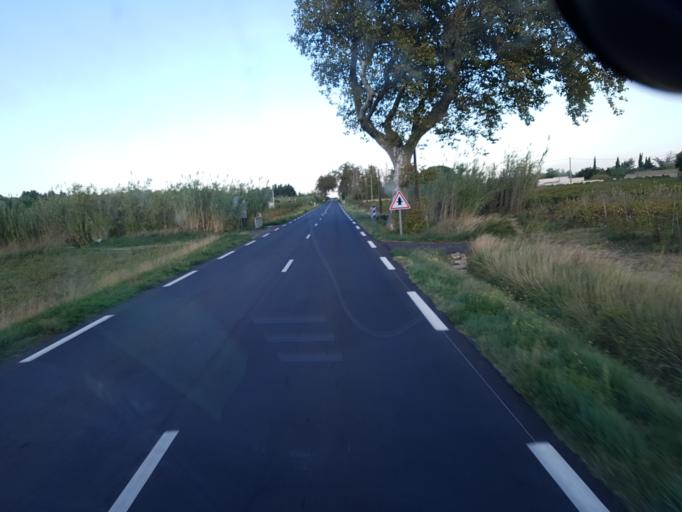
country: FR
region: Languedoc-Roussillon
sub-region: Departement de l'Aude
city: Leucate
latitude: 42.9621
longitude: 2.9905
